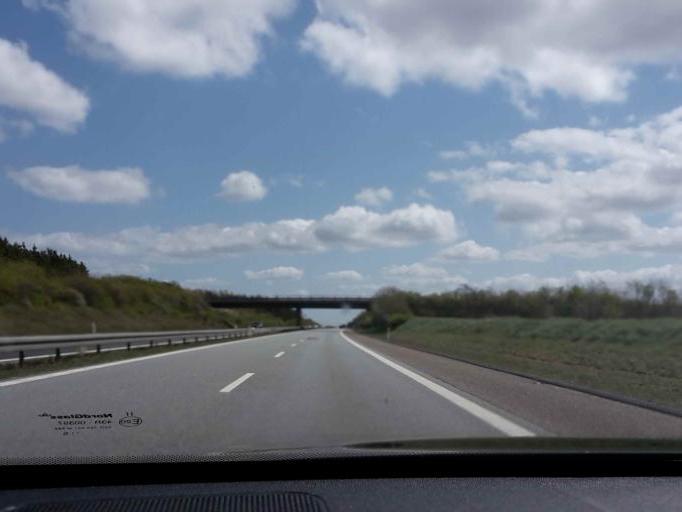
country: DK
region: South Denmark
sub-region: Vejen Kommune
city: Holsted
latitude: 55.5179
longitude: 8.9335
